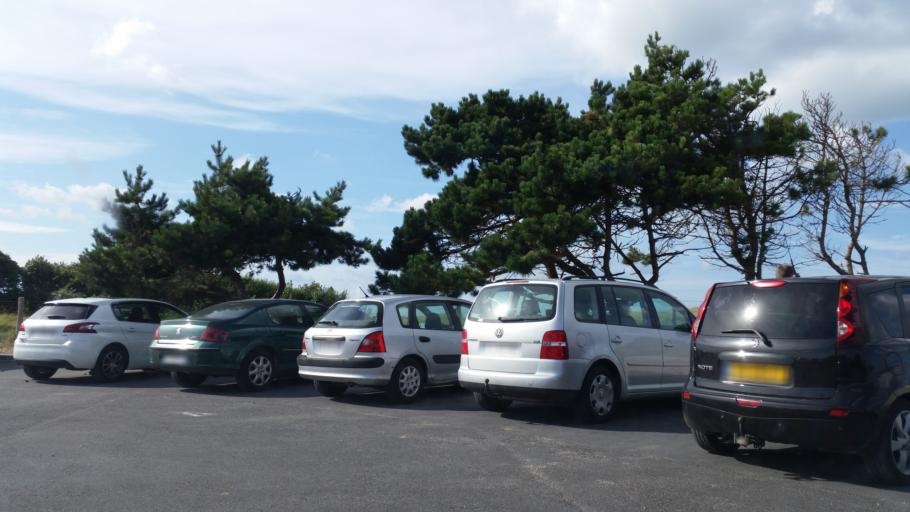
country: FR
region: Lower Normandy
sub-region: Departement de la Manche
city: Sainte-Mere-Eglise
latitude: 49.4437
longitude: -1.2097
